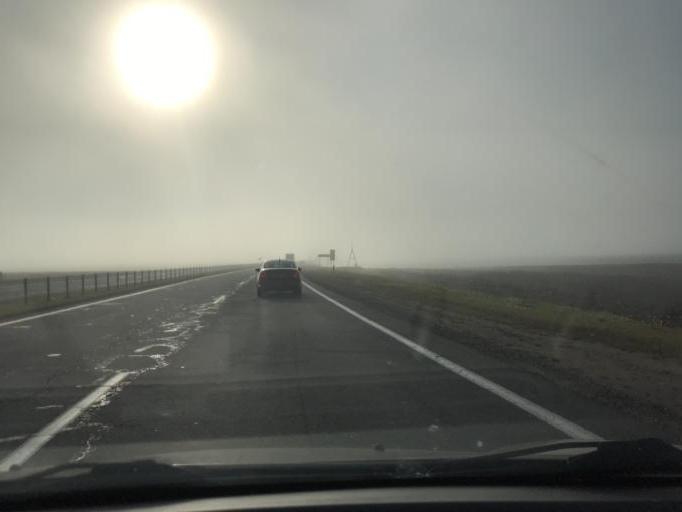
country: BY
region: Minsk
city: Dukora
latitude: 53.6759
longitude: 27.9301
